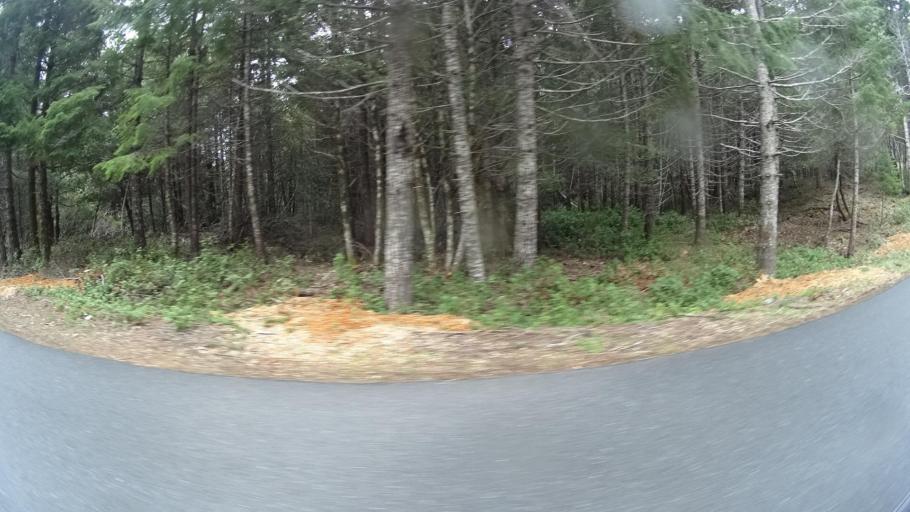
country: US
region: California
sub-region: Humboldt County
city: Willow Creek
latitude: 41.2020
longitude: -123.8009
